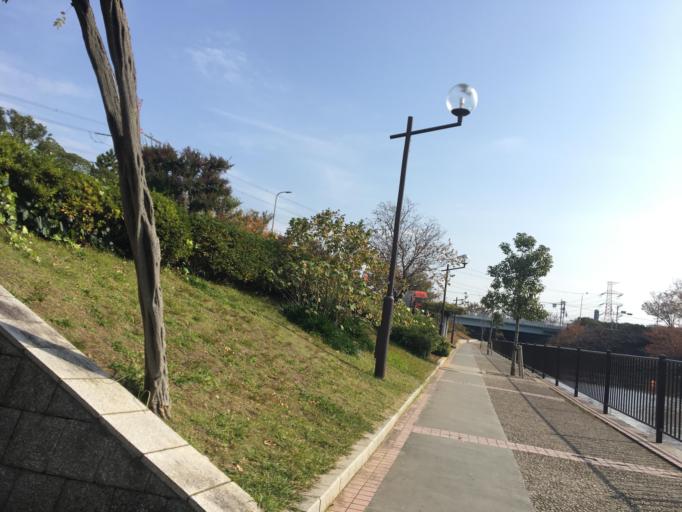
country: JP
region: Tokyo
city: Urayasu
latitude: 35.6540
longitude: 139.8620
